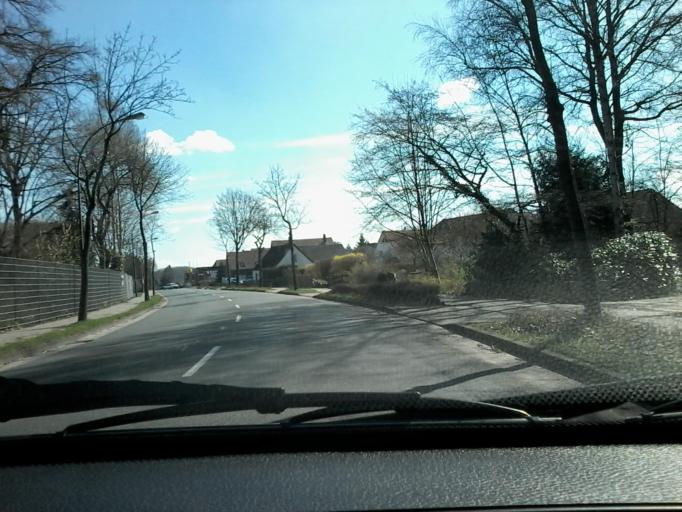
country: DE
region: Lower Saxony
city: Ahsen-Oetzen
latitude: 52.9987
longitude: 9.0885
